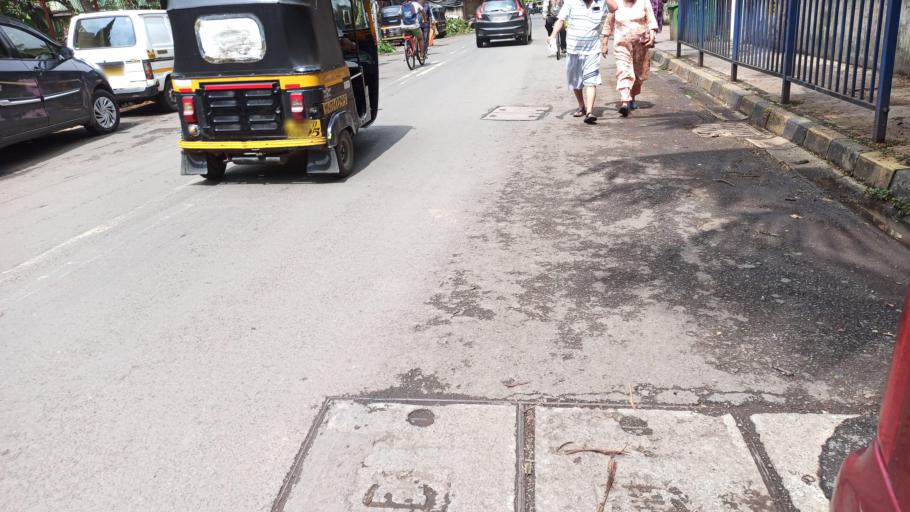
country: IN
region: Maharashtra
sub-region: Mumbai Suburban
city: Borivli
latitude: 19.2593
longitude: 72.8605
